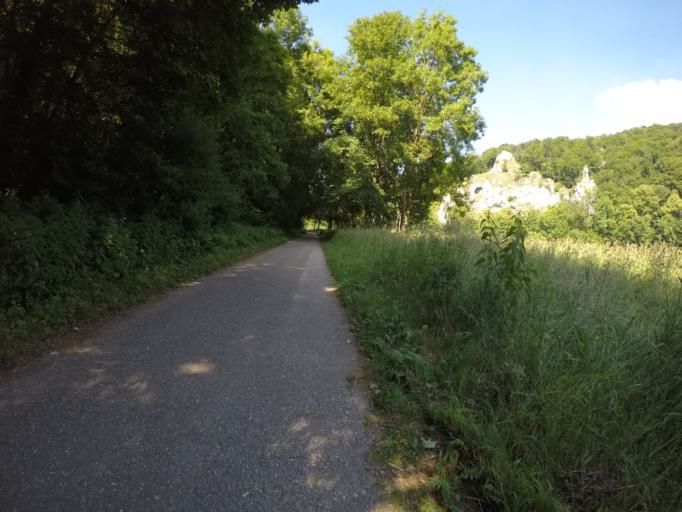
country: DE
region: Bavaria
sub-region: Lower Bavaria
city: Ihrlerstein
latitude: 48.9082
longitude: 11.8508
